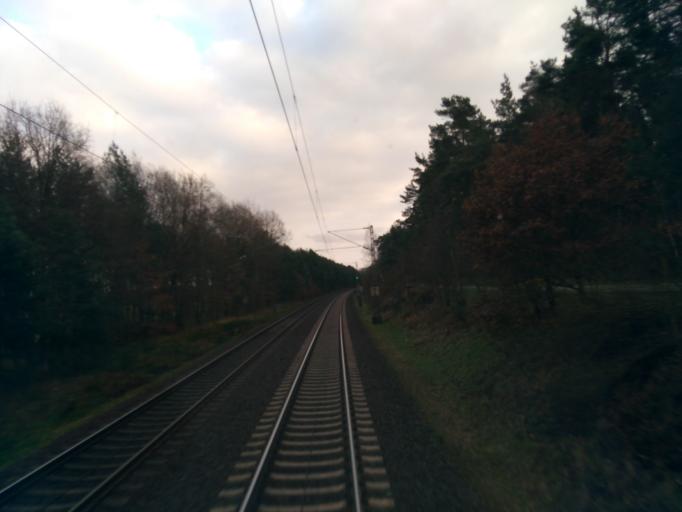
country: DE
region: Lower Saxony
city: Bienenbuttel
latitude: 53.1296
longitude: 10.5094
